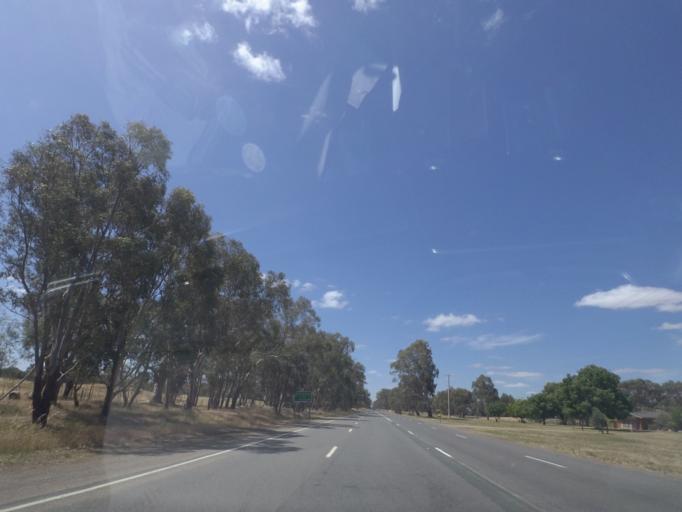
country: AU
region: Victoria
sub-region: Wangaratta
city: Wangaratta
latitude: -36.4280
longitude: 146.2557
